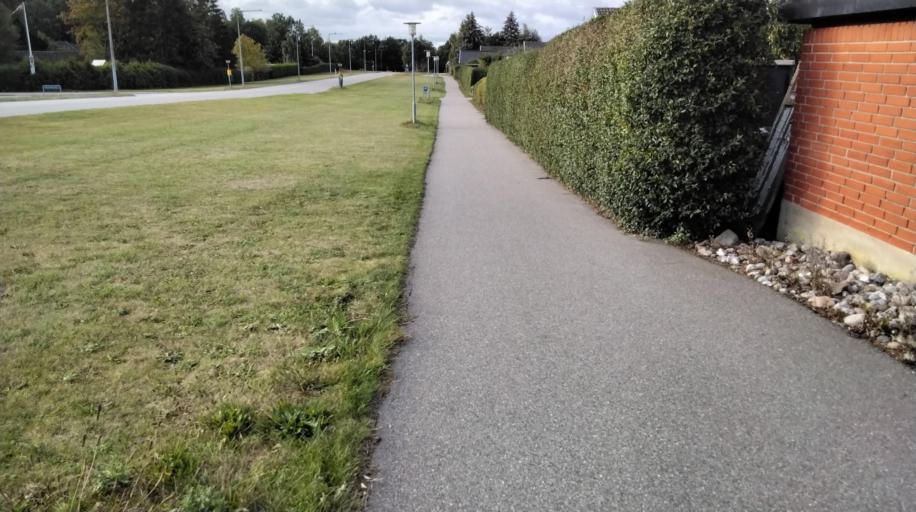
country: DK
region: Zealand
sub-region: Naestved Kommune
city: Naestved
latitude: 55.2254
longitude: 11.7375
